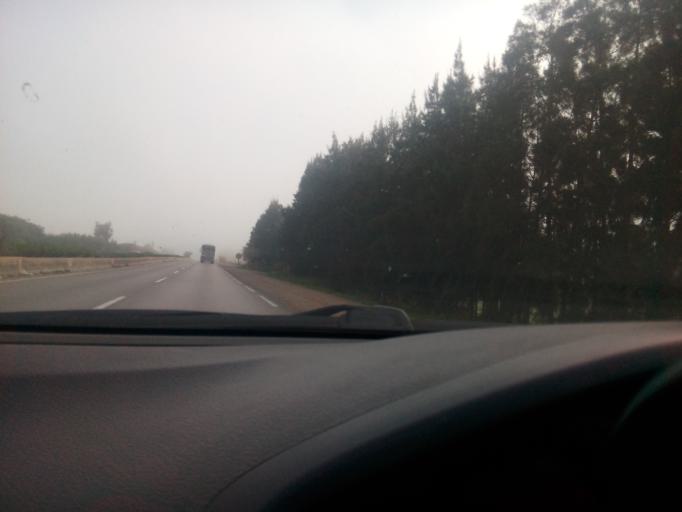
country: DZ
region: Oran
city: Mers el Kebir
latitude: 35.6047
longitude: -0.7588
